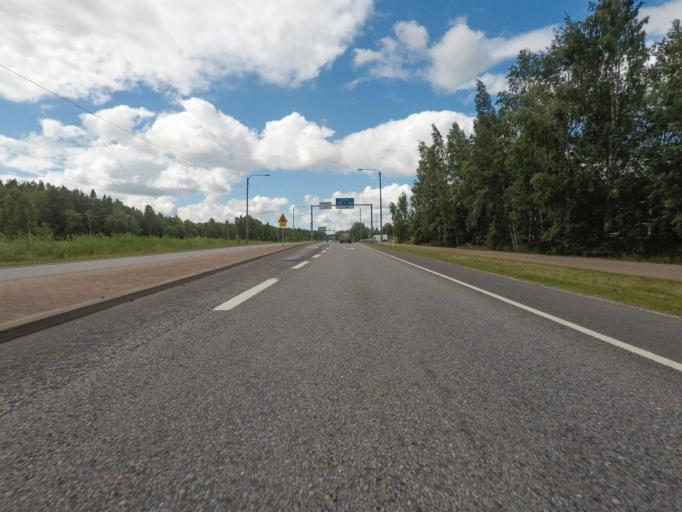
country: FI
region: Varsinais-Suomi
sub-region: Turku
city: Raisio
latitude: 60.4714
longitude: 22.1429
